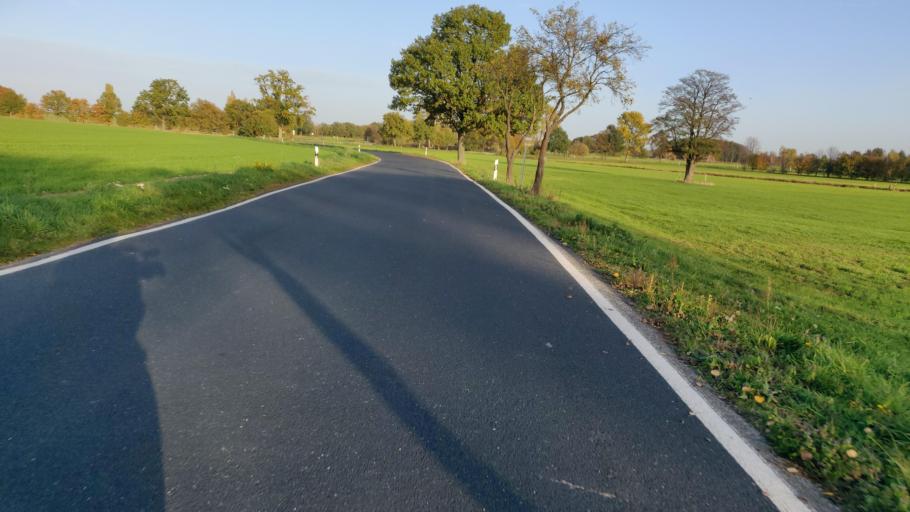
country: DE
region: Brandenburg
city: Hirschfeld
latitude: 51.3421
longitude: 13.5825
